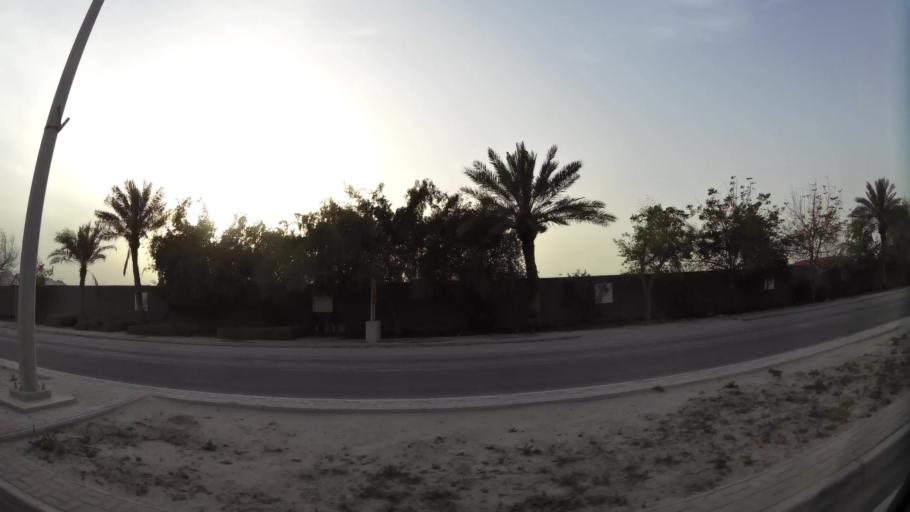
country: QA
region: Baladiyat ad Dawhah
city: Doha
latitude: 25.3460
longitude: 51.5240
